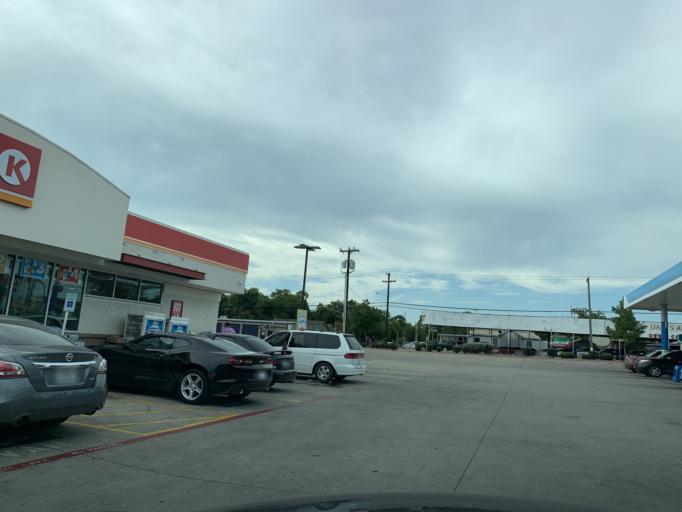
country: US
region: Texas
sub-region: Dallas County
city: Cockrell Hill
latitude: 32.7502
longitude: -96.8772
